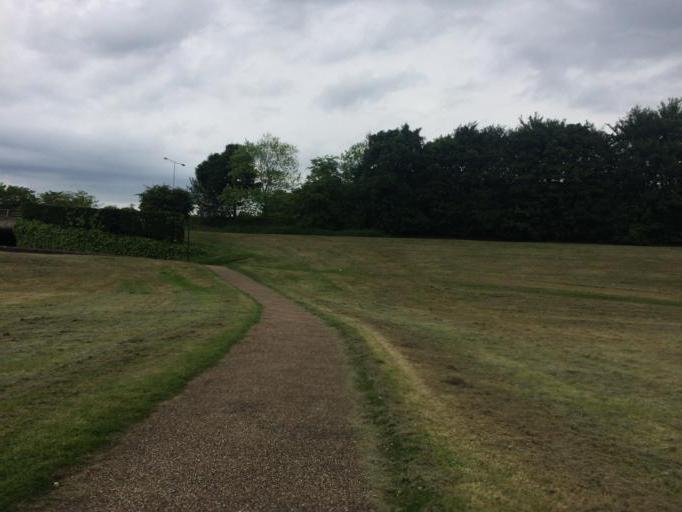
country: GB
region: England
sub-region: Milton Keynes
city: Loughton
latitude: 52.0289
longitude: -0.7716
